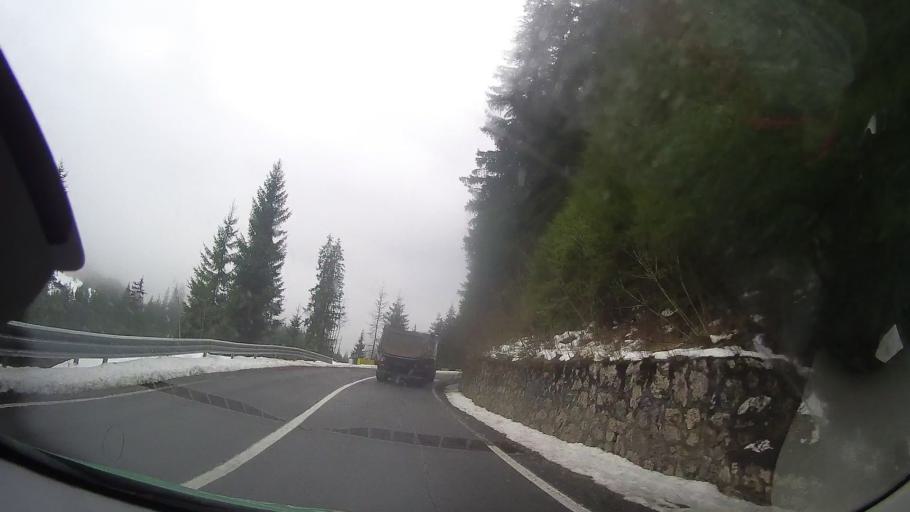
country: RO
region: Neamt
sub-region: Comuna Bicaz Chei
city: Bicaz Chei
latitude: 46.7798
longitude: 25.7471
